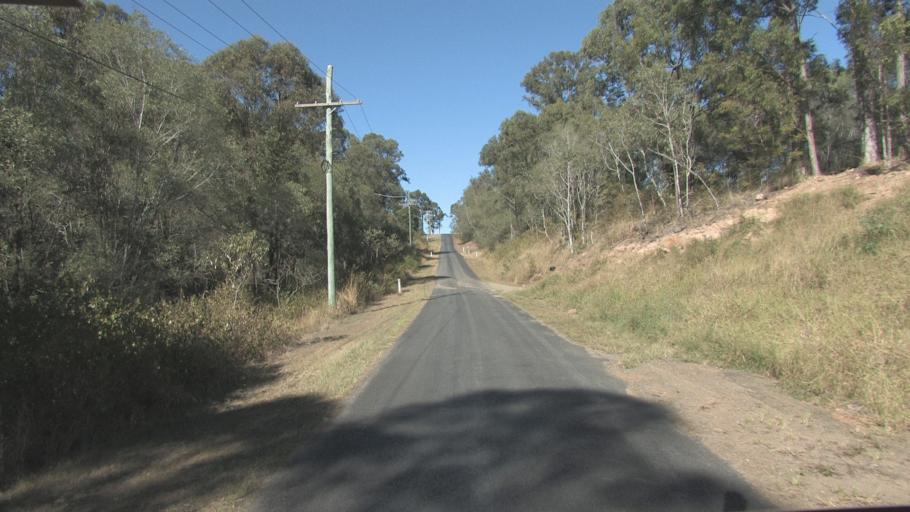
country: AU
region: Queensland
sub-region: Logan
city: Cedar Vale
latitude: -27.8985
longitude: 153.0216
